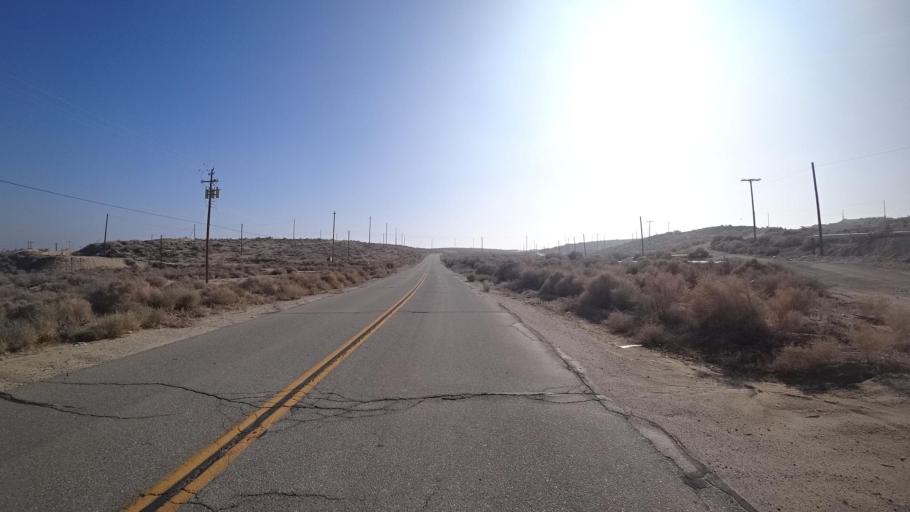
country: US
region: California
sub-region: Kern County
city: Taft Heights
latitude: 35.1508
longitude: -119.5172
